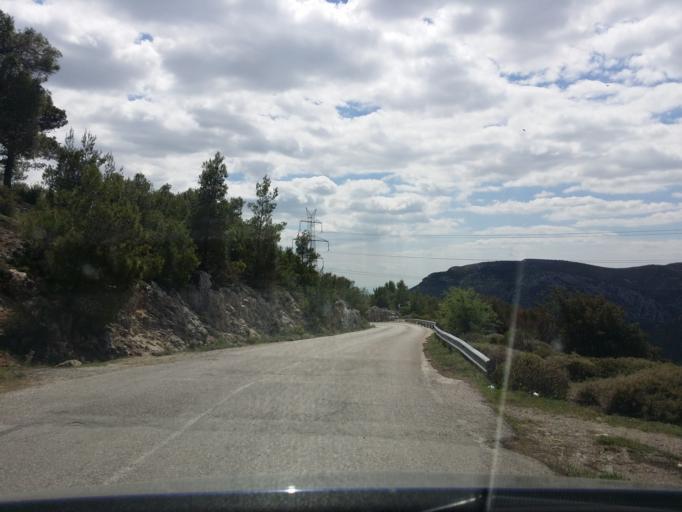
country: GR
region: Attica
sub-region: Nomarchia Dytikis Attikis
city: Fyli
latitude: 38.1334
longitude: 23.6491
